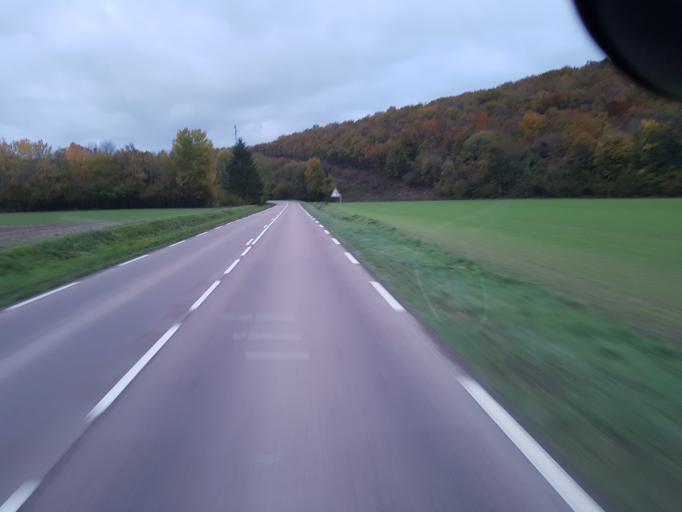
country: FR
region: Champagne-Ardenne
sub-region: Departement de l'Aube
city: Mussy-sur-Seine
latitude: 48.0087
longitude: 4.4742
